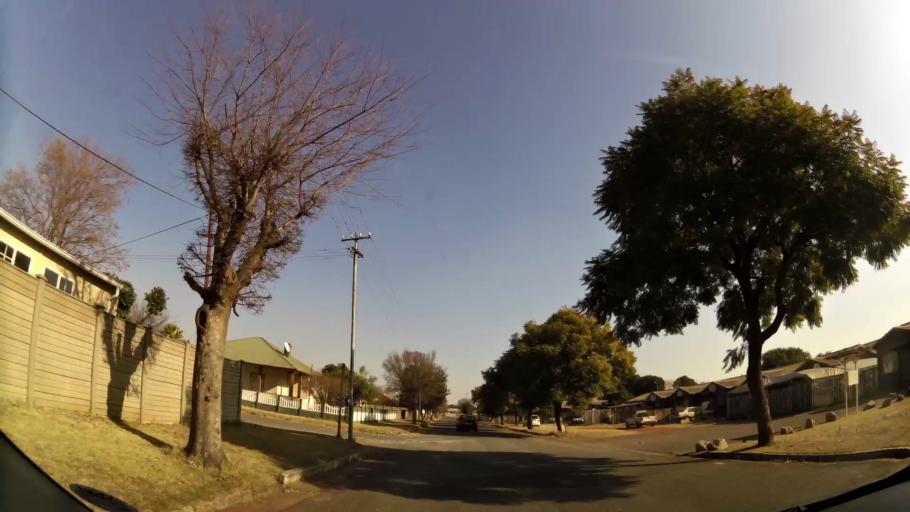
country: ZA
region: Gauteng
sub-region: West Rand District Municipality
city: Randfontein
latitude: -26.1710
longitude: 27.7107
